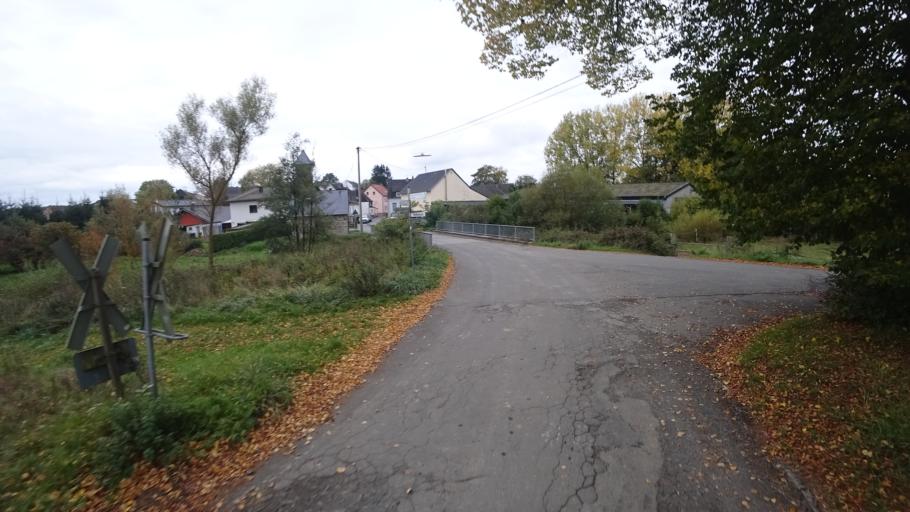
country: DE
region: Rheinland-Pfalz
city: Dierdorf
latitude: 50.5381
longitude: 7.6629
